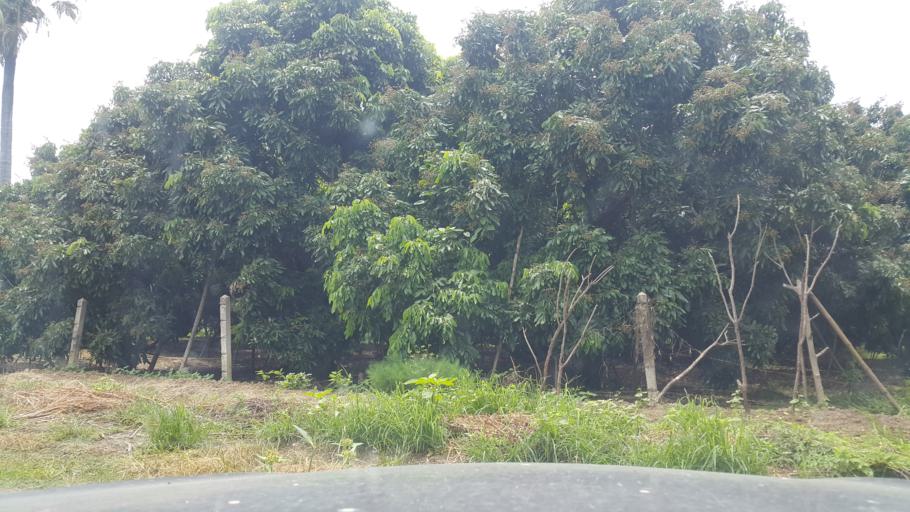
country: TH
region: Chiang Mai
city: San Kamphaeng
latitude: 18.7008
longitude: 99.1658
